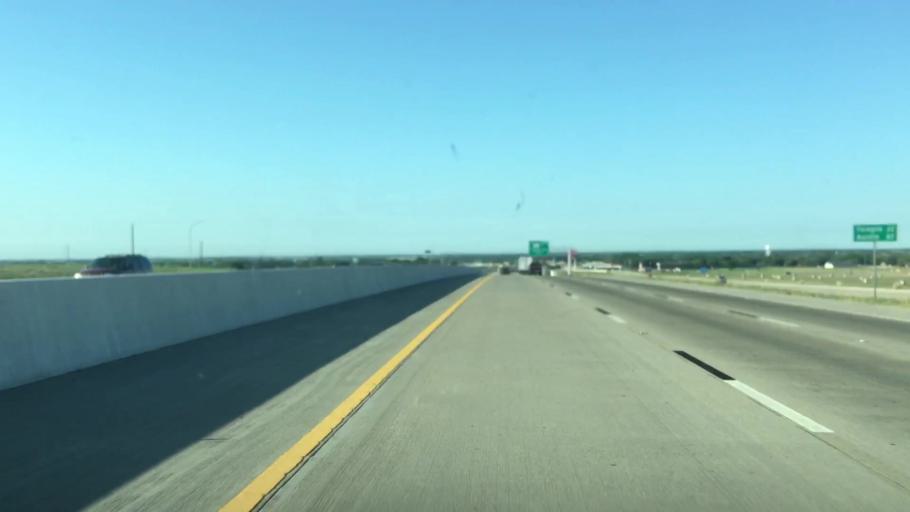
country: US
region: Texas
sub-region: McLennan County
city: Lorena
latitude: 31.4003
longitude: -97.2077
